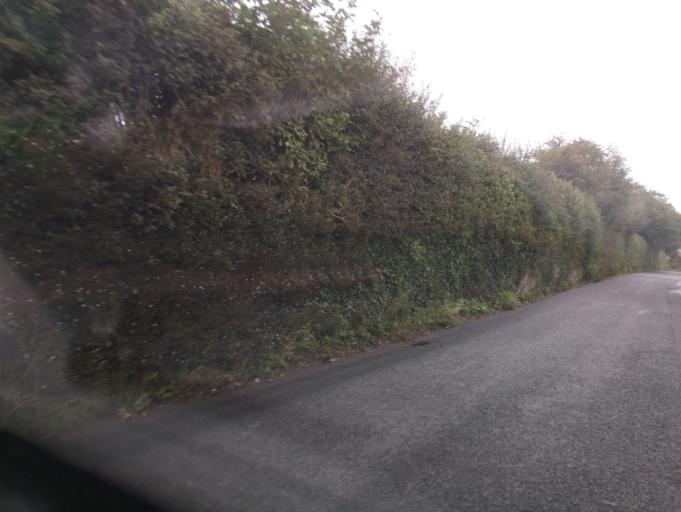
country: GB
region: England
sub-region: Devon
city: Salcombe
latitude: 50.2731
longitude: -3.6879
